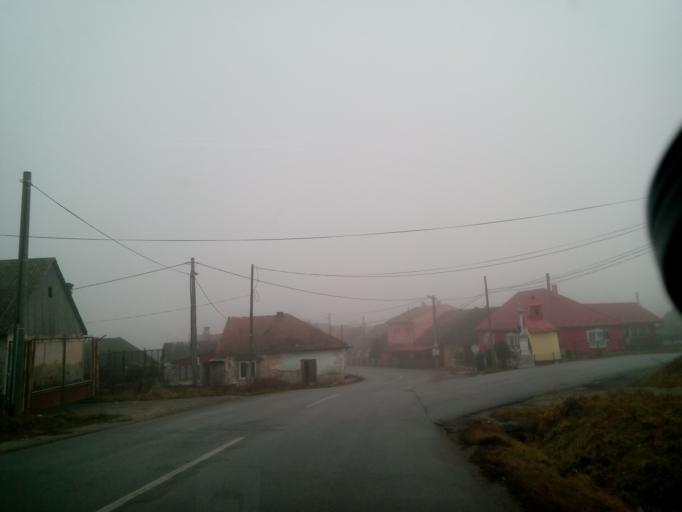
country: SK
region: Presovsky
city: Spisske Podhradie
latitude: 48.9688
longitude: 20.7836
